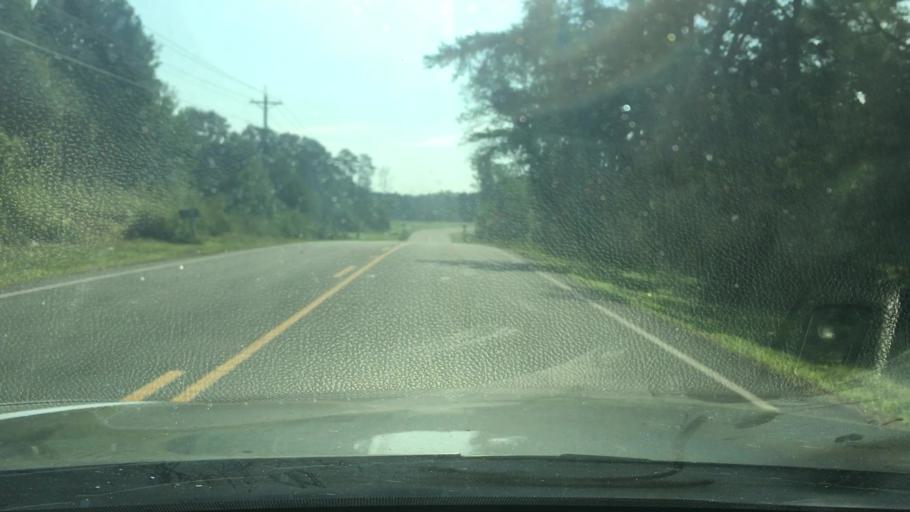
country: US
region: North Carolina
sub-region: Caswell County
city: Yanceyville
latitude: 36.2807
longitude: -79.3531
